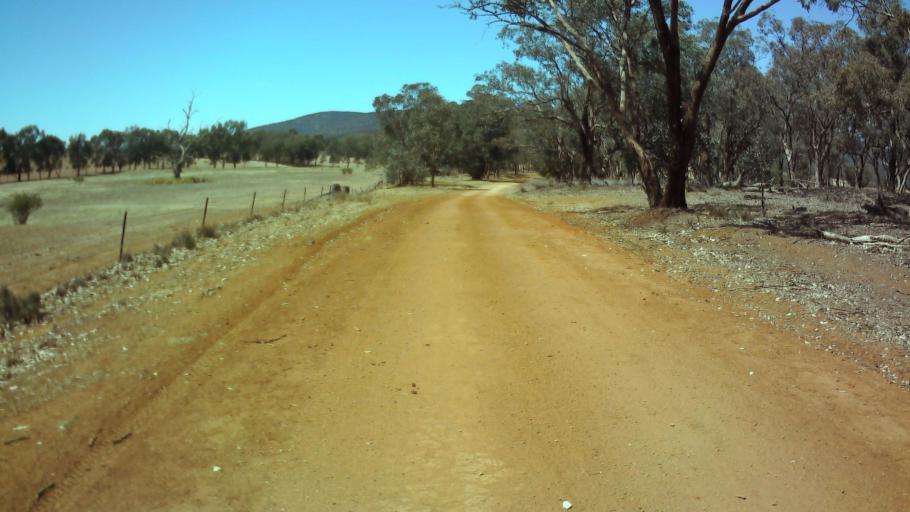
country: AU
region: New South Wales
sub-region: Weddin
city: Grenfell
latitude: -33.9523
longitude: 148.0846
